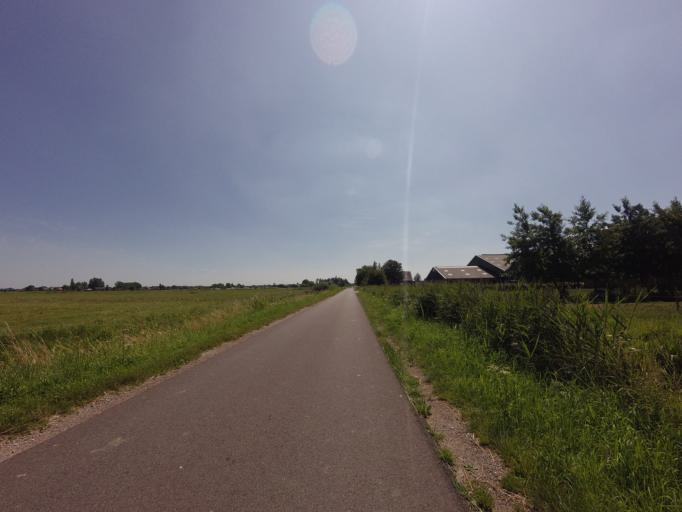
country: NL
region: Utrecht
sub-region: Stichtse Vecht
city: Maarssen
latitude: 52.1648
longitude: 5.0639
